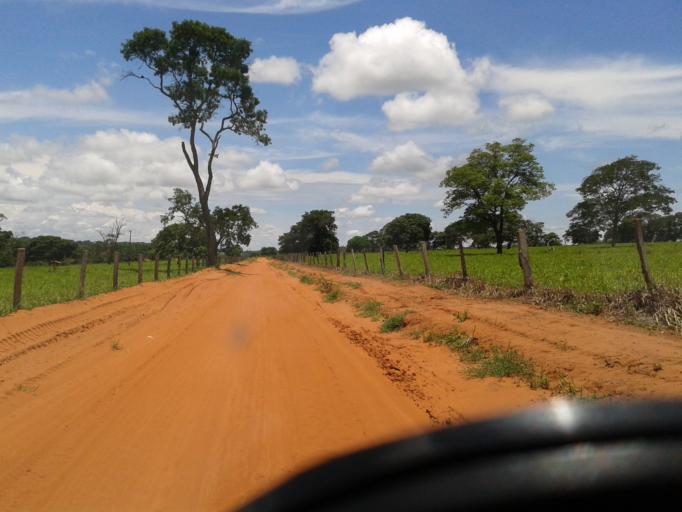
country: BR
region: Minas Gerais
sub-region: Santa Vitoria
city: Santa Vitoria
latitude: -18.9394
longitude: -49.8599
